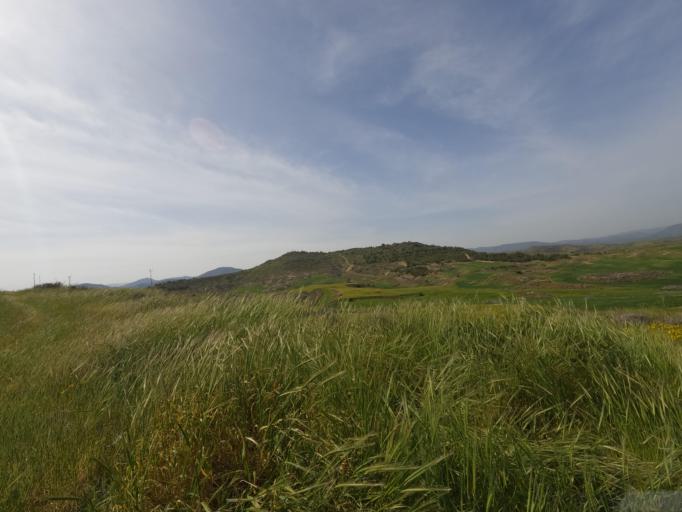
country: CY
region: Lefkosia
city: Astromeritis
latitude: 35.0987
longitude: 32.9605
